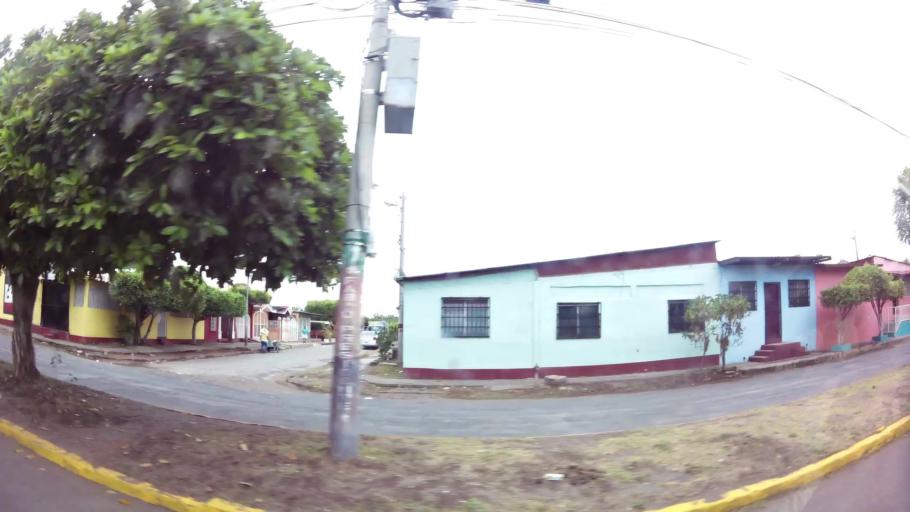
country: NI
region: Granada
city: Granada
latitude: 11.9420
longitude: -85.9505
